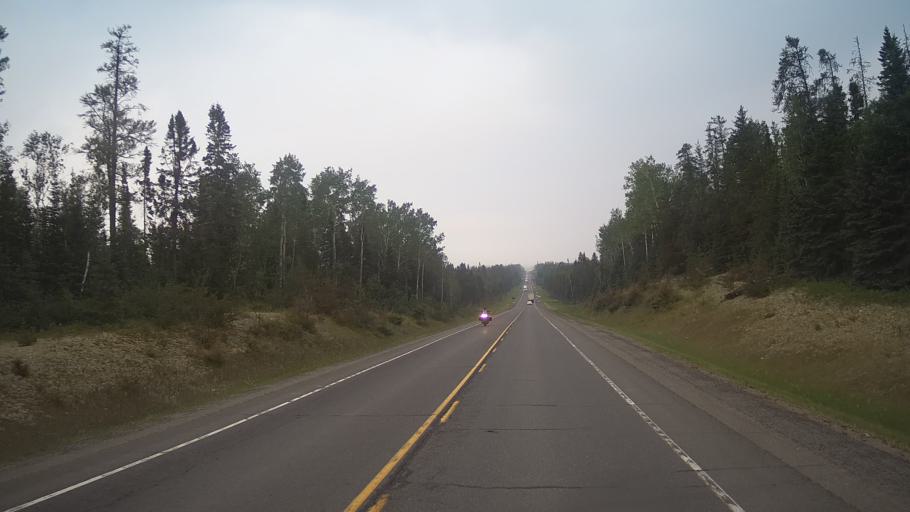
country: CA
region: Ontario
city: Greenstone
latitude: 49.1958
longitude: -88.2142
